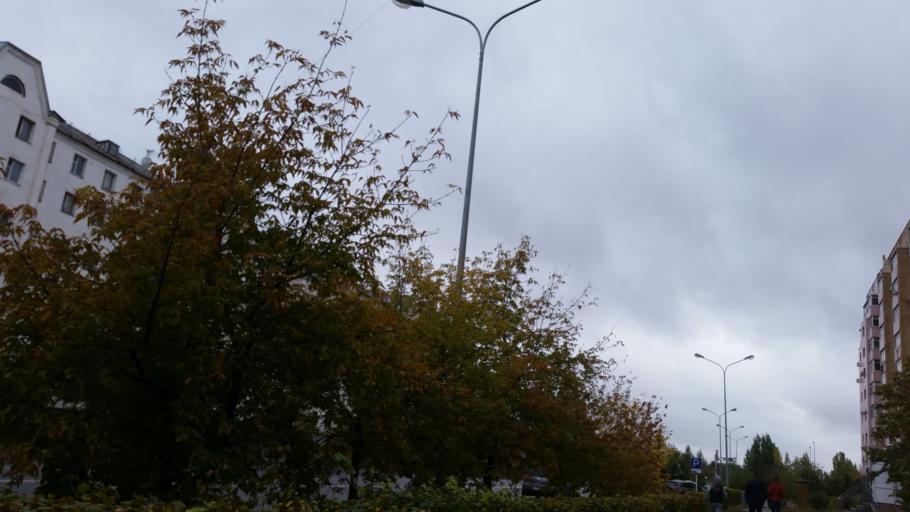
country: KZ
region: Astana Qalasy
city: Astana
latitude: 51.1514
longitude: 71.4996
